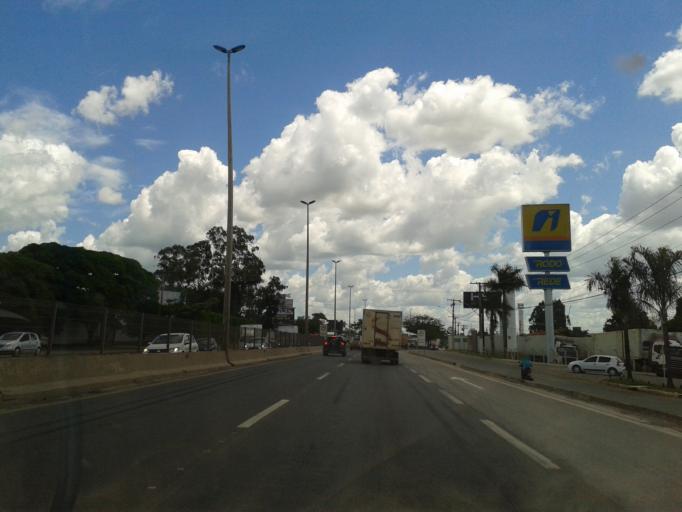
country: BR
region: Goias
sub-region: Goiania
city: Goiania
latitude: -16.7434
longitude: -49.2413
